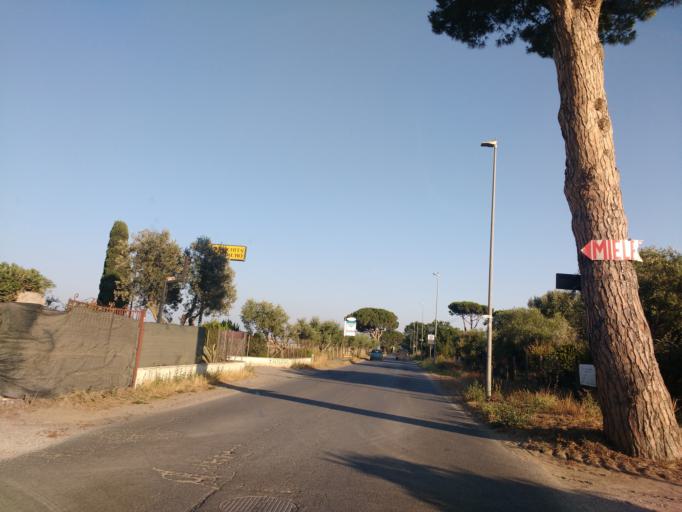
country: IT
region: Latium
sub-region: Citta metropolitana di Roma Capitale
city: Fregene
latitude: 41.8494
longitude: 12.2191
